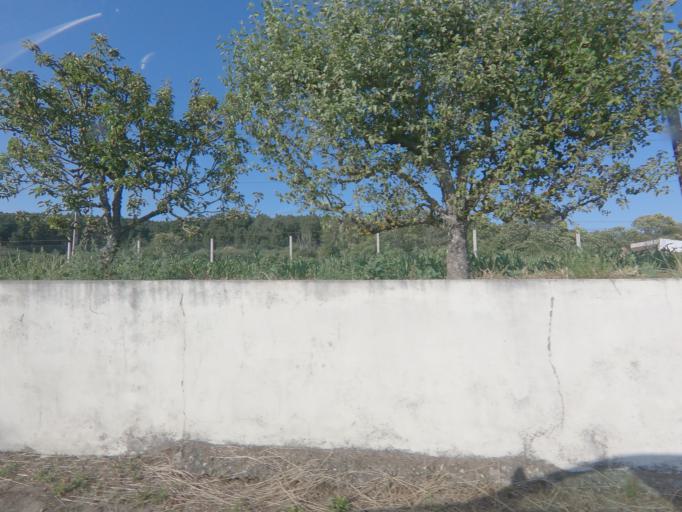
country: PT
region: Vila Real
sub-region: Sabrosa
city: Vilela
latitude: 41.2250
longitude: -7.6029
